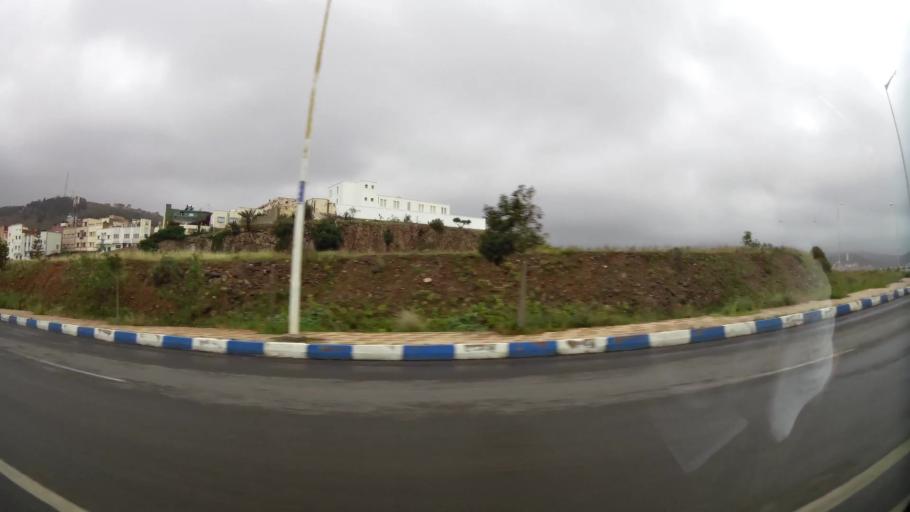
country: MA
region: Oriental
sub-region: Nador
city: Nador
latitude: 35.1891
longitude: -2.9258
